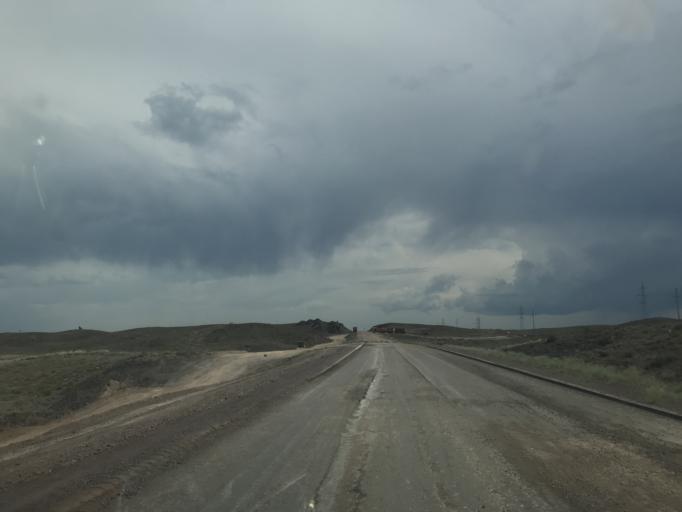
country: KZ
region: Zhambyl
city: Mynaral
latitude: 45.2849
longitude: 73.7749
